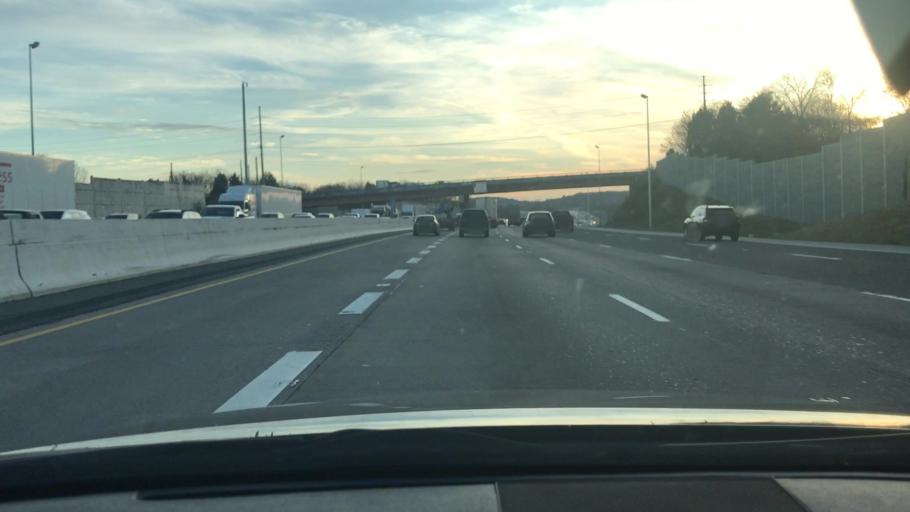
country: US
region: Tennessee
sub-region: Davidson County
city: Goodlettsville
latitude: 36.2991
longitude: -86.7126
